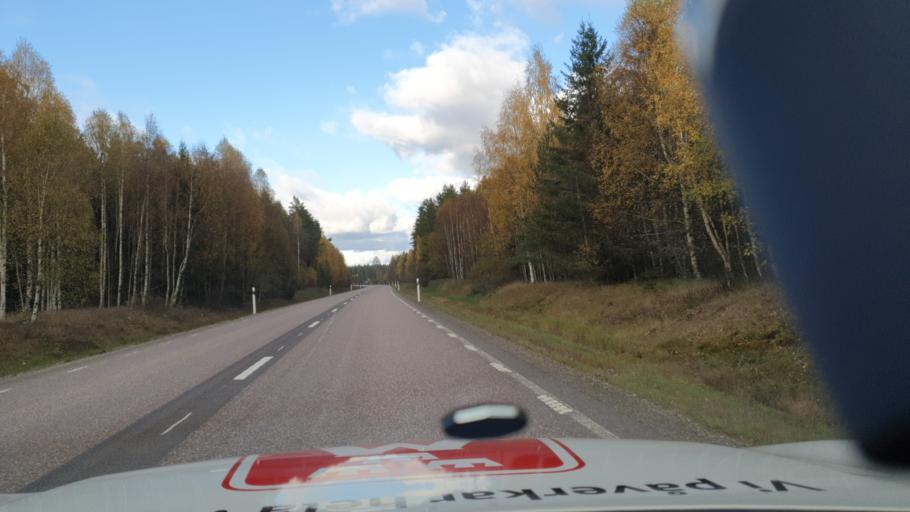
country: SE
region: Gaevleborg
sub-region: Gavle Kommun
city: Hedesunda
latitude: 60.3815
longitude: 16.9721
